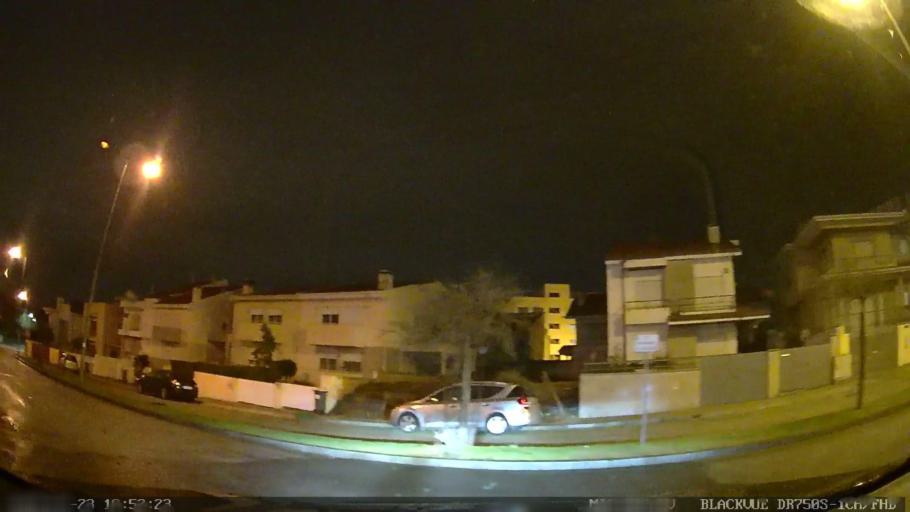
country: PT
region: Porto
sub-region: Maia
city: Maia
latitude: 41.2376
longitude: -8.6484
